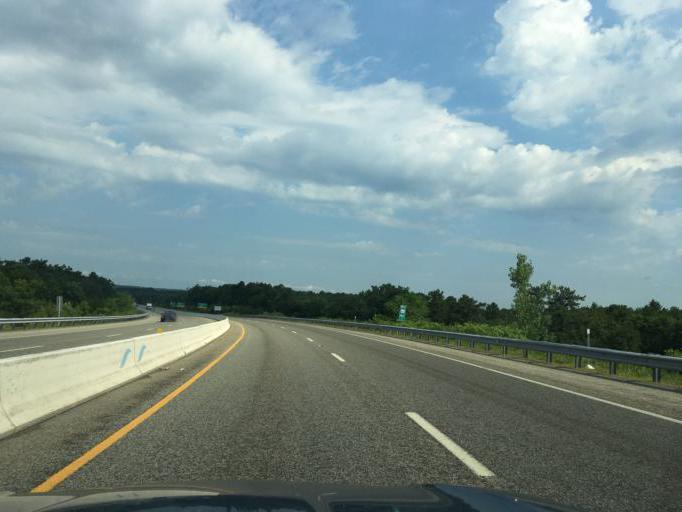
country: US
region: Rhode Island
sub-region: Kent County
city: East Greenwich
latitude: 41.6218
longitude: -71.4719
